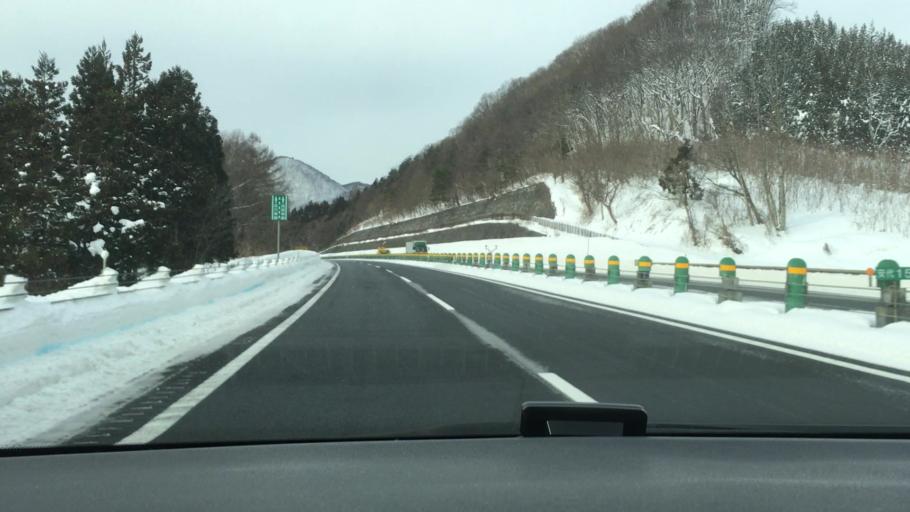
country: JP
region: Akita
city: Hanawa
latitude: 40.1364
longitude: 140.9701
